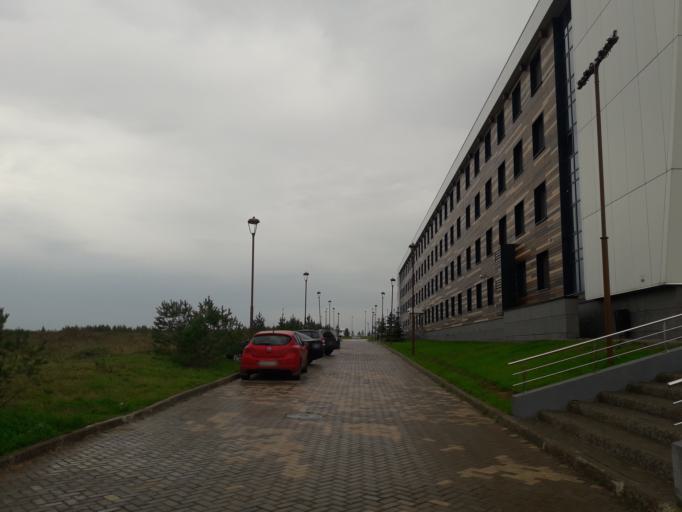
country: RU
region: Tatarstan
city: Sviyazhsk
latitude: 55.7536
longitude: 48.7400
